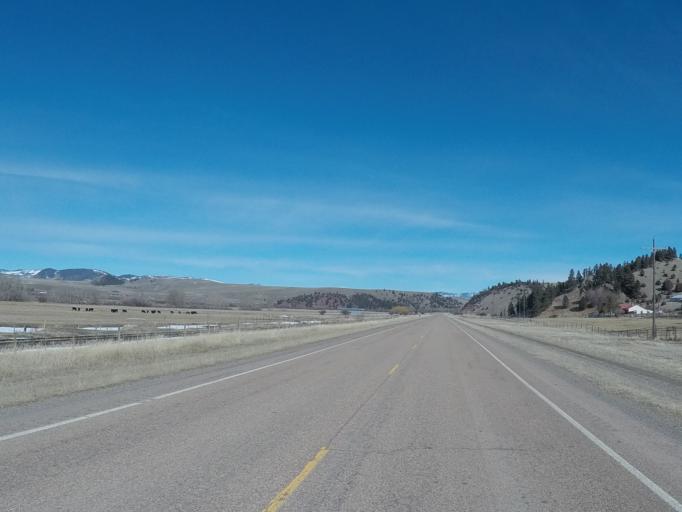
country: US
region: Montana
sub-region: Granite County
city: Philipsburg
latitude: 46.4982
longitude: -113.2227
